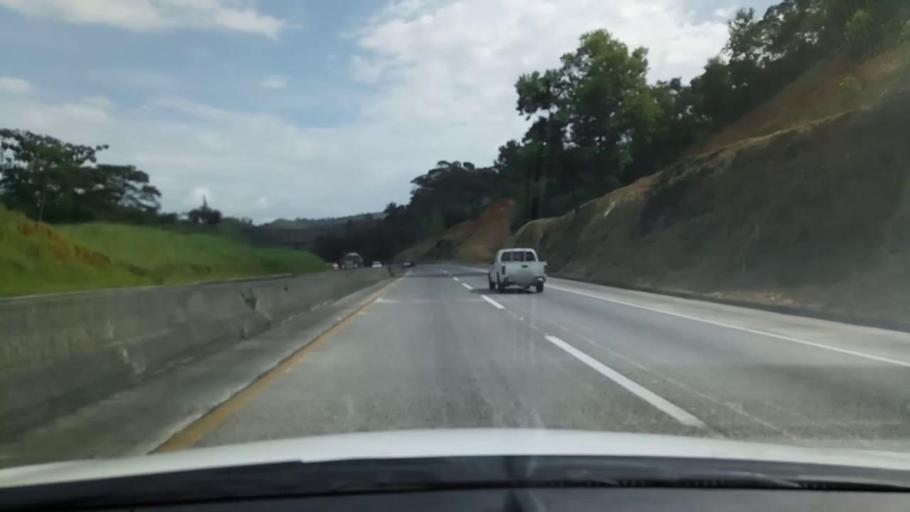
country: PA
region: Colon
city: Quebrada Bonita Adentro
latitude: 9.2775
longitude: -79.7256
